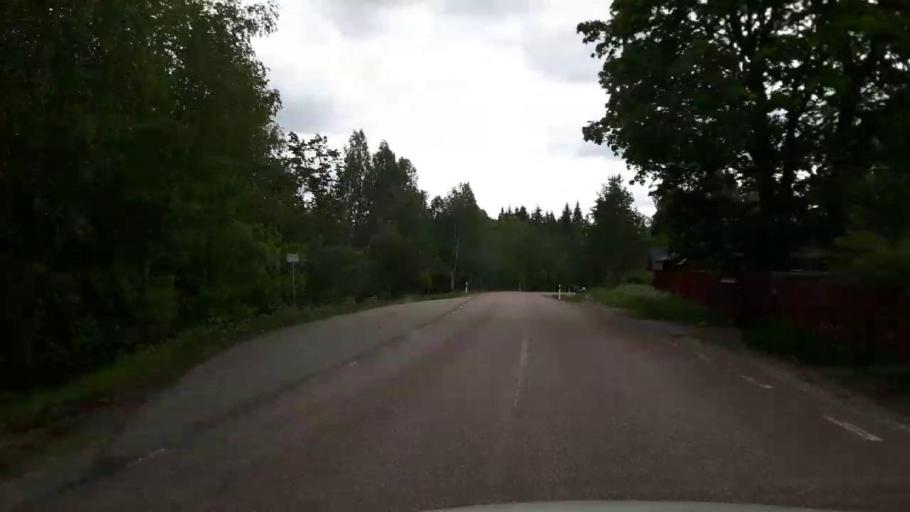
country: SE
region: Vaestmanland
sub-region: Skinnskattebergs Kommun
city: Skinnskatteberg
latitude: 59.8393
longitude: 15.8413
